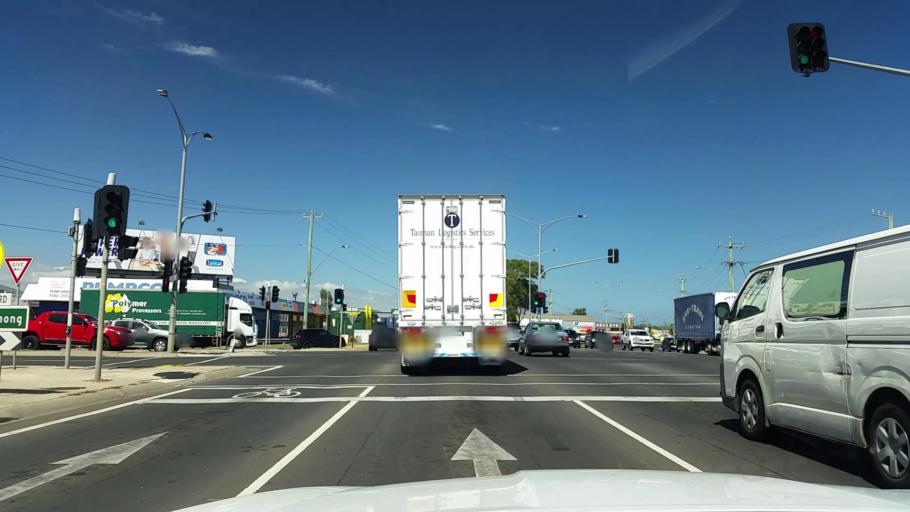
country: AU
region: Victoria
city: Heatherton
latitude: -37.9862
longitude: 145.1095
